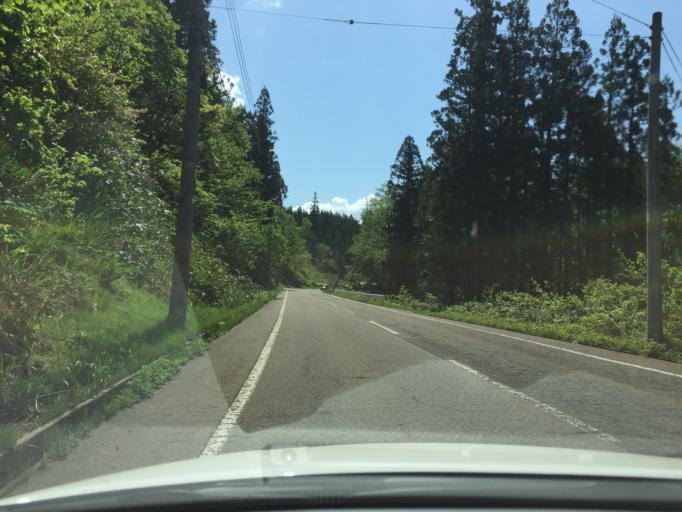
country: JP
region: Niigata
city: Tochio-honcho
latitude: 37.5319
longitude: 139.0929
